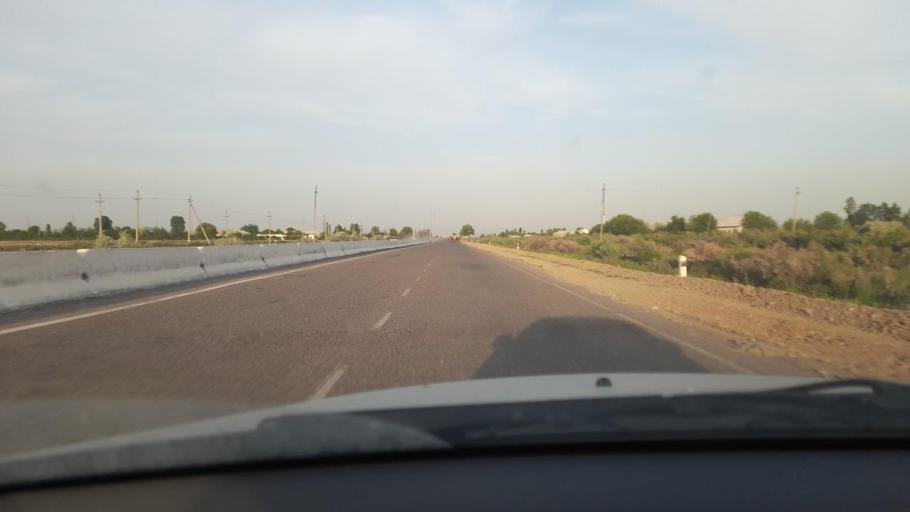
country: UZ
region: Sirdaryo
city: Guliston
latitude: 40.4952
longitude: 68.6404
